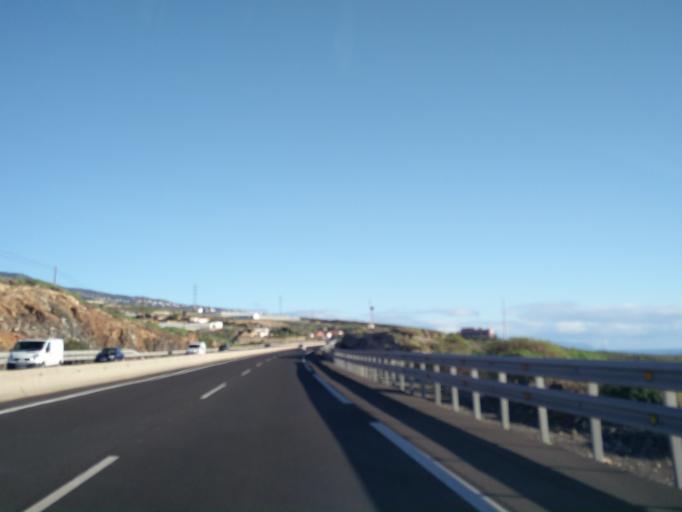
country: ES
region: Canary Islands
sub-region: Provincia de Santa Cruz de Tenerife
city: Fasnia
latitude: 28.2076
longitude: -16.4255
